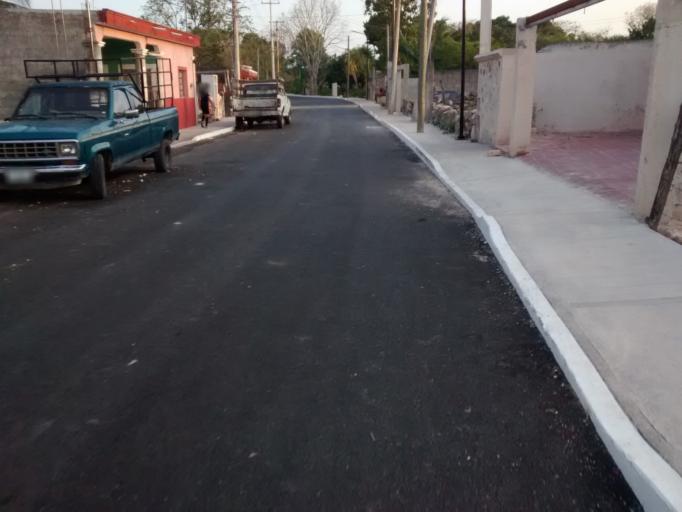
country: MX
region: Yucatan
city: Valladolid
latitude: 20.6835
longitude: -88.1932
